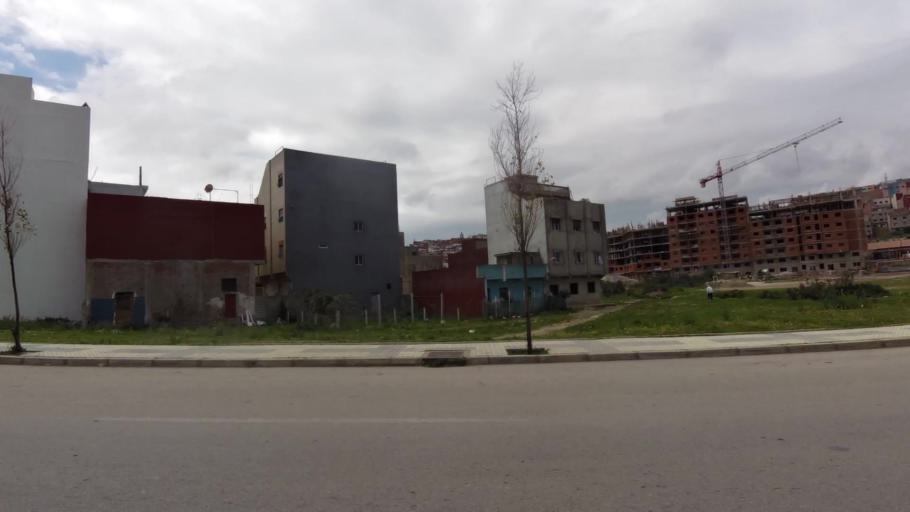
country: MA
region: Tanger-Tetouan
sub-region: Tanger-Assilah
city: Boukhalef
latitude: 35.7587
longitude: -5.8540
